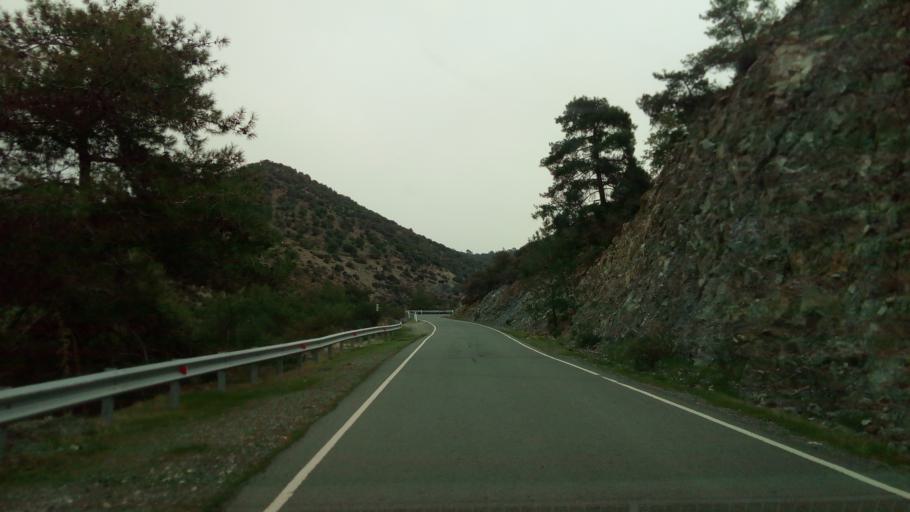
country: CY
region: Limassol
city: Mouttagiaka
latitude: 34.7763
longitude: 33.0820
